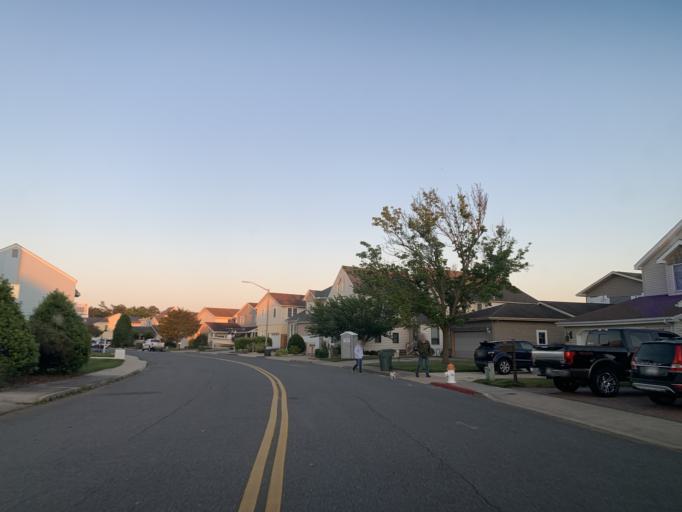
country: US
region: Delaware
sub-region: Sussex County
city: Bethany Beach
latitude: 38.4483
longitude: -75.0655
